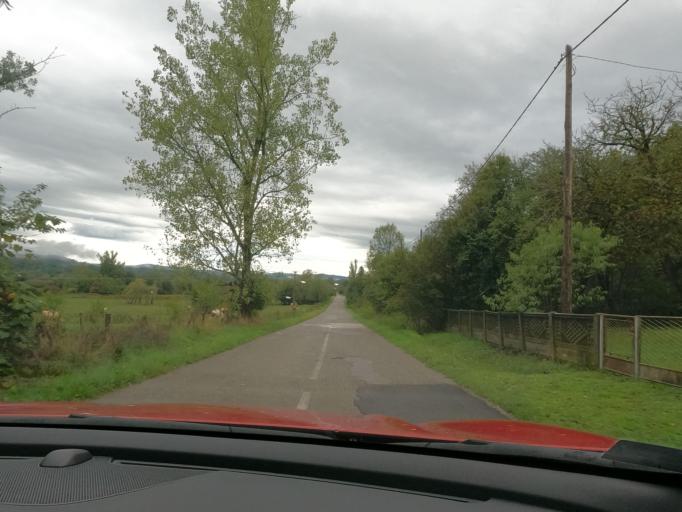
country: HR
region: Sisacko-Moslavacka
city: Glina
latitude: 45.3142
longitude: 16.1955
